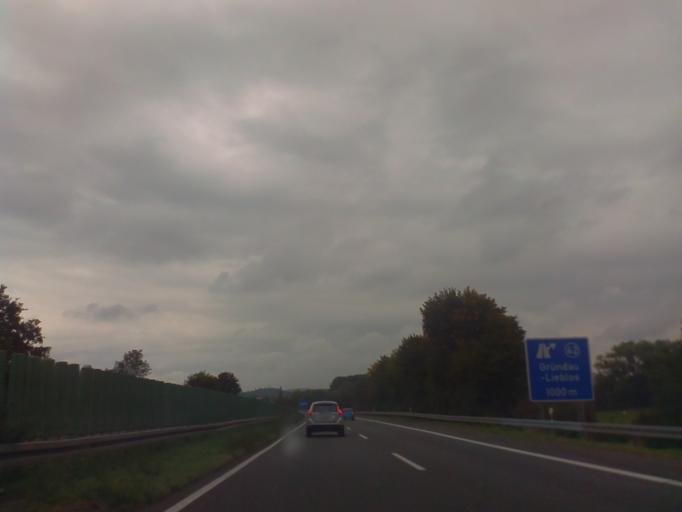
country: DE
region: Hesse
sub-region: Regierungsbezirk Darmstadt
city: Gelnhausen
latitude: 50.1955
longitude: 9.1545
